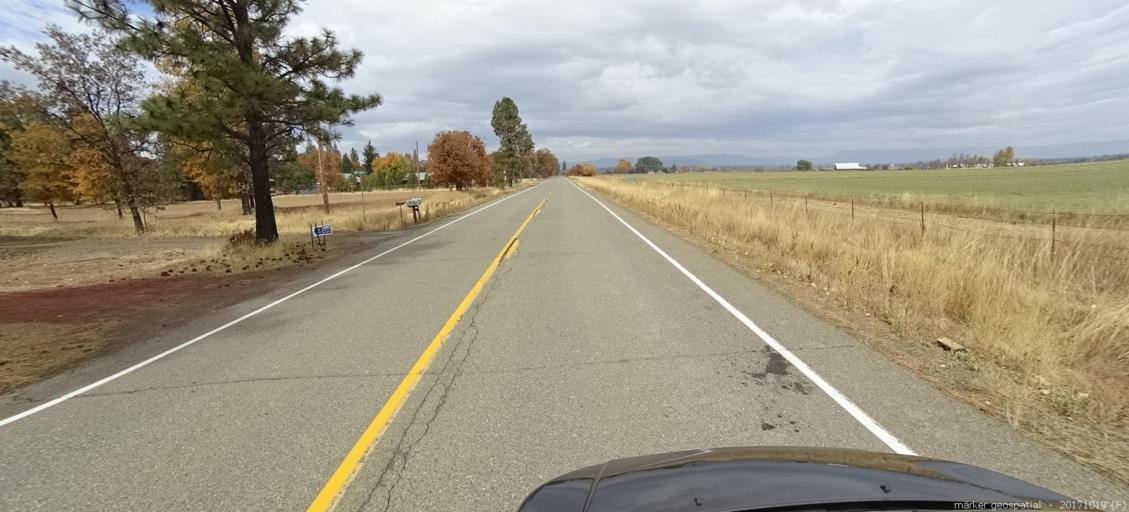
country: US
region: California
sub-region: Shasta County
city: Burney
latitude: 41.0832
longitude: -121.5144
